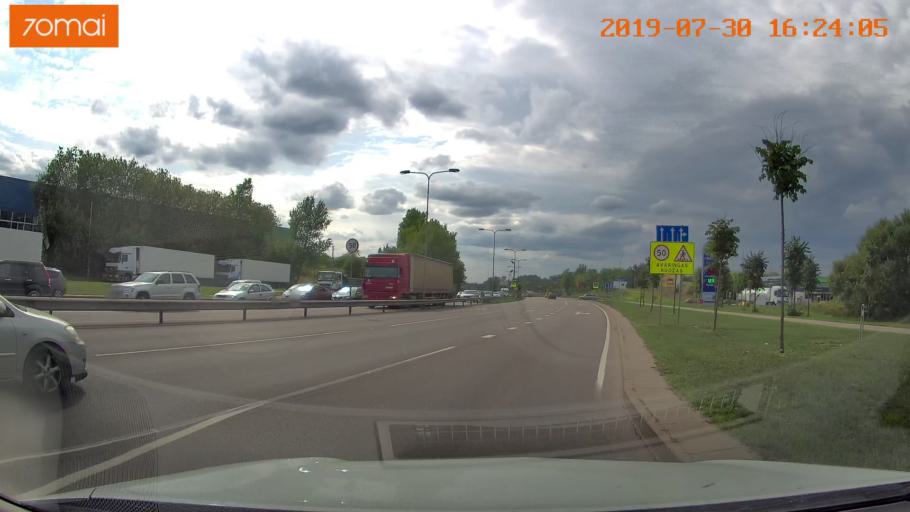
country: LT
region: Vilnius County
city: Rasos
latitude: 54.6561
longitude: 25.2935
